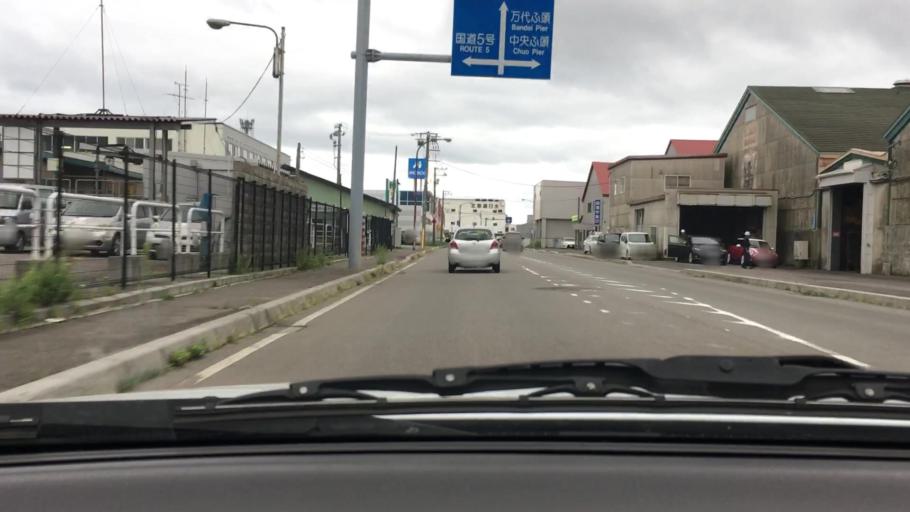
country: JP
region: Hokkaido
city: Hakodate
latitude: 41.7881
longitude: 140.7282
